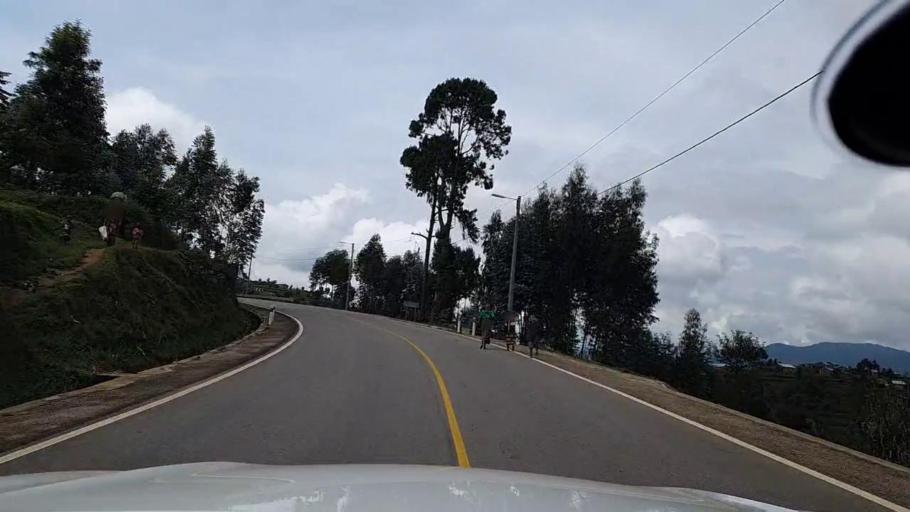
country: RW
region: Southern Province
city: Nzega
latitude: -2.5252
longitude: 29.4515
